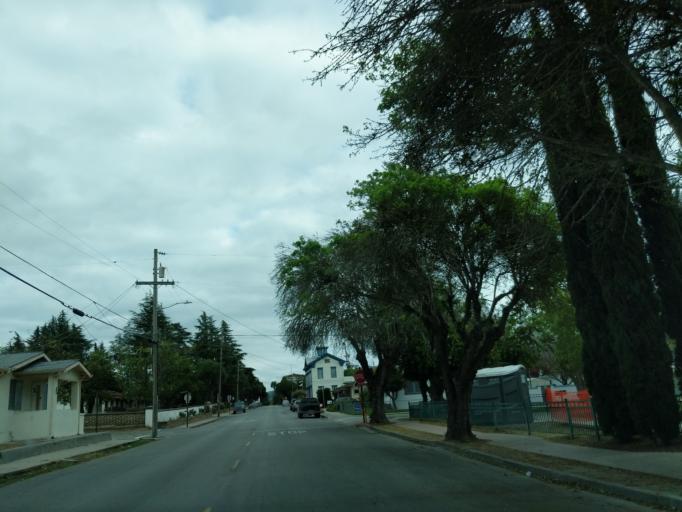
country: US
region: California
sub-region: San Benito County
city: San Juan Bautista
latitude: 36.8469
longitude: -121.5390
